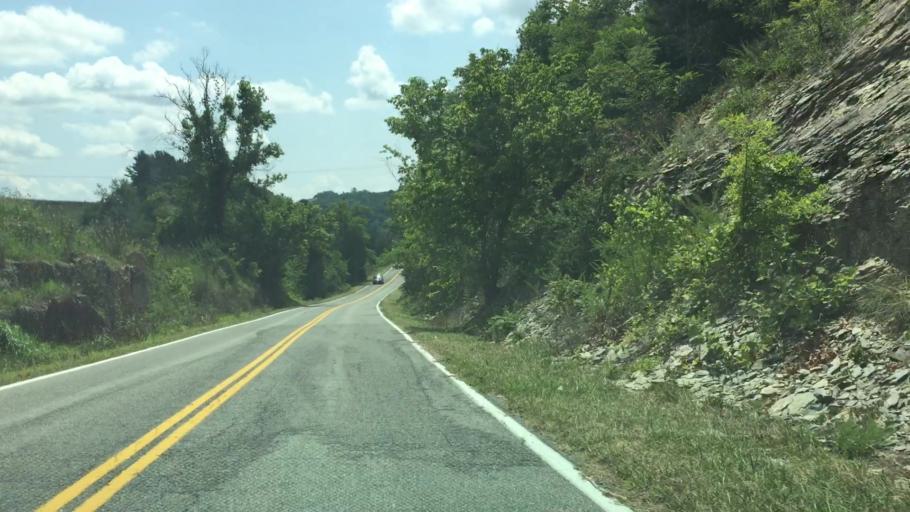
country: US
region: Virginia
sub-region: Pulaski County
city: Pulaski
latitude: 37.0063
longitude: -80.7552
